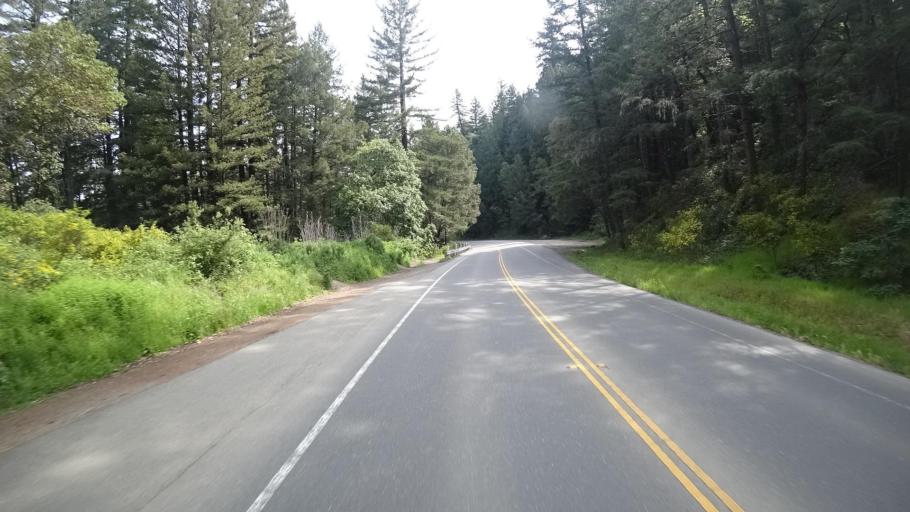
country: US
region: California
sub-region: Humboldt County
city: Redway
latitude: 40.1256
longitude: -123.8231
